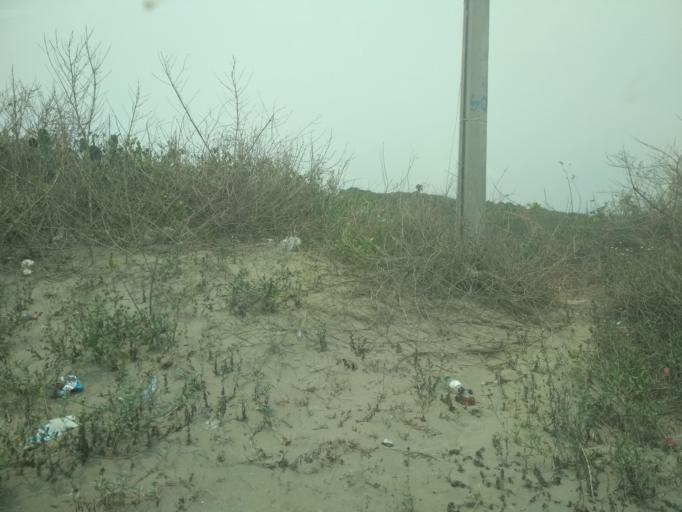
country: MX
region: Veracruz
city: Anton Lizardo
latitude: 19.0536
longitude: -96.0337
